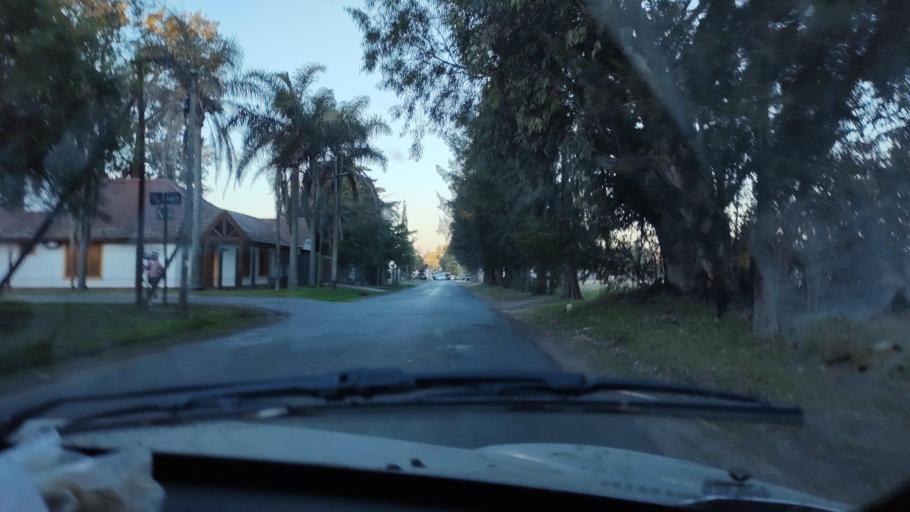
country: AR
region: Buenos Aires
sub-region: Partido de La Plata
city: La Plata
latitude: -34.9038
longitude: -58.0464
